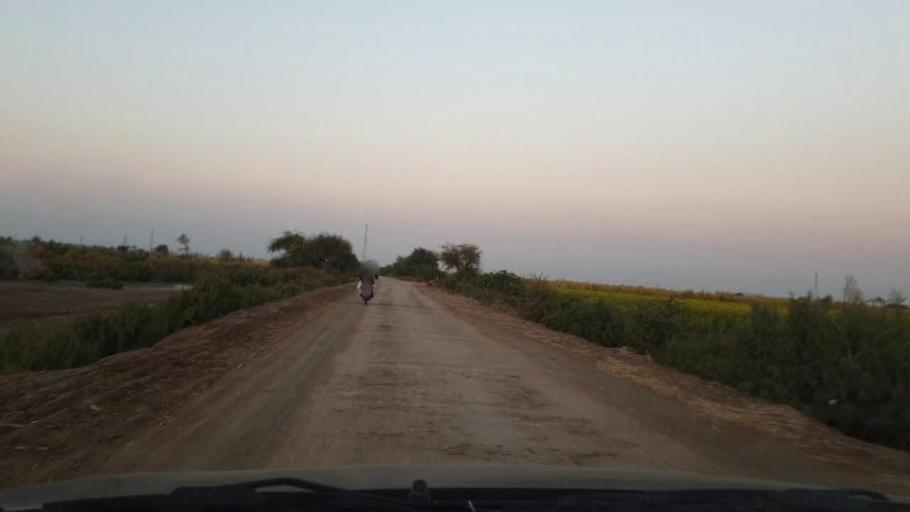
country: PK
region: Sindh
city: Jhol
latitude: 25.9453
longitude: 68.9743
